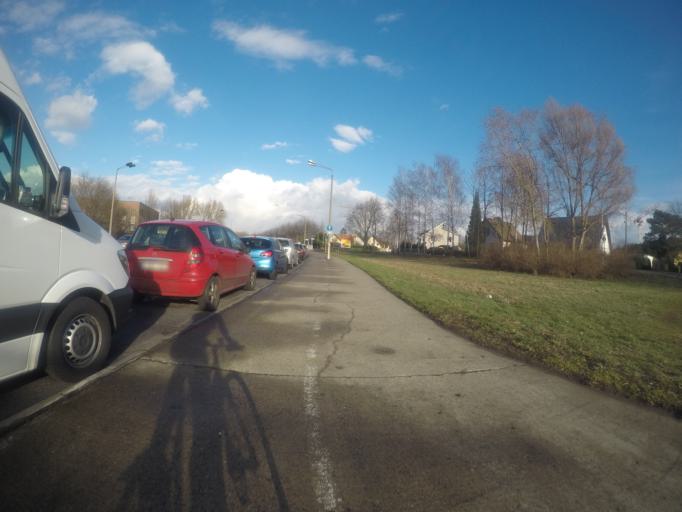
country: DE
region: Berlin
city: Kaulsdorf
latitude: 52.5132
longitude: 13.5795
